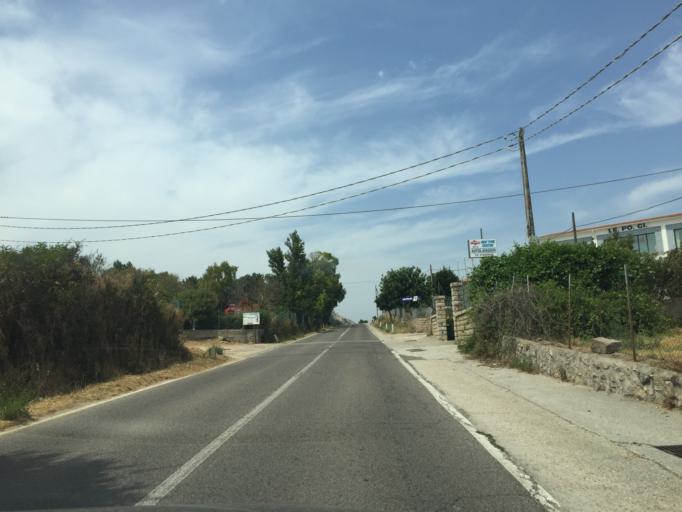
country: IT
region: Sardinia
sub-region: Provincia di Olbia-Tempio
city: Aggius
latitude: 40.9211
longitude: 9.0715
